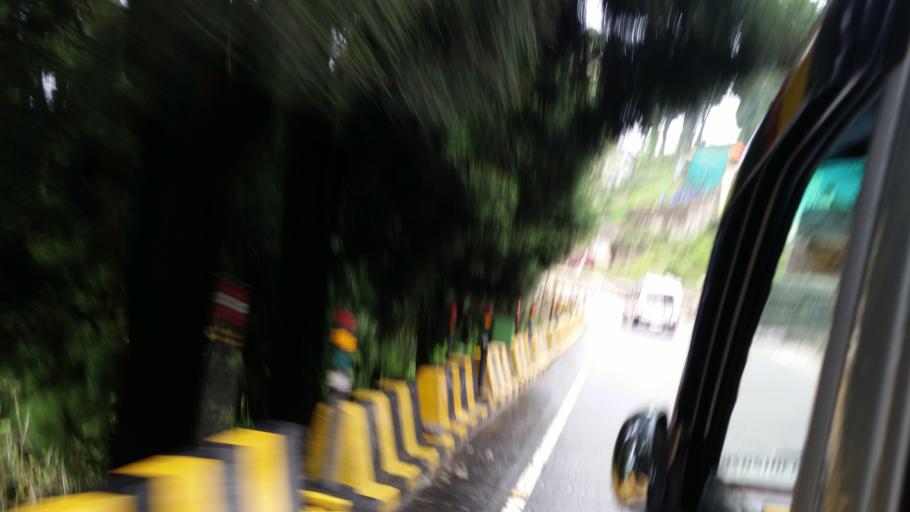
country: IN
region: West Bengal
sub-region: Darjiling
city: Darjiling
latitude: 27.0185
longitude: 88.2498
